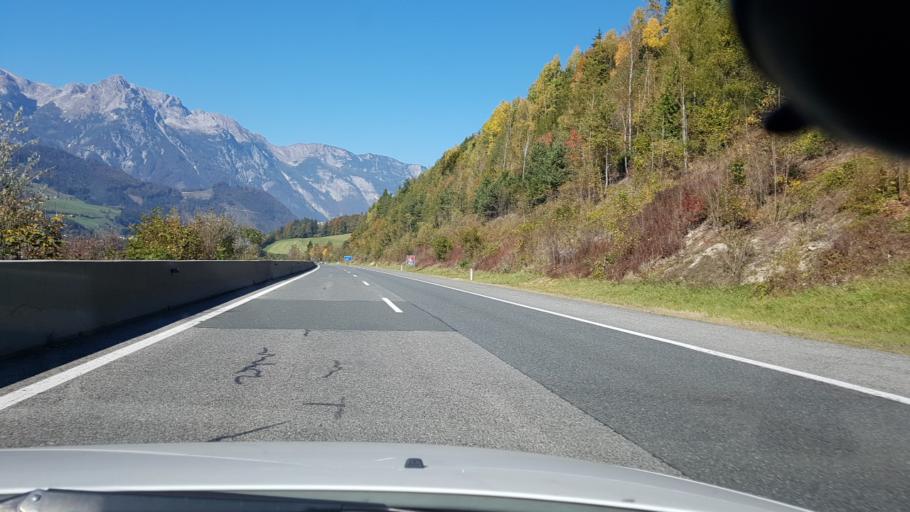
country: AT
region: Salzburg
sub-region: Politischer Bezirk Sankt Johann im Pongau
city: Pfarrwerfen
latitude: 47.4535
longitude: 13.2161
